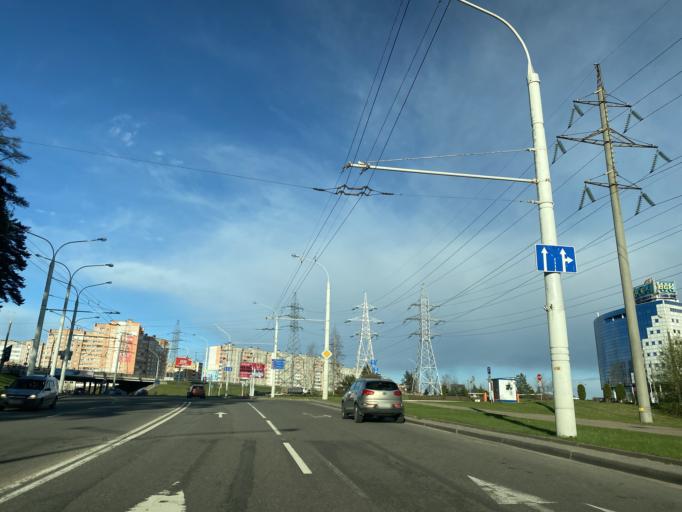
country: BY
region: Minsk
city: Borovlyany
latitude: 53.9449
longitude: 27.6630
